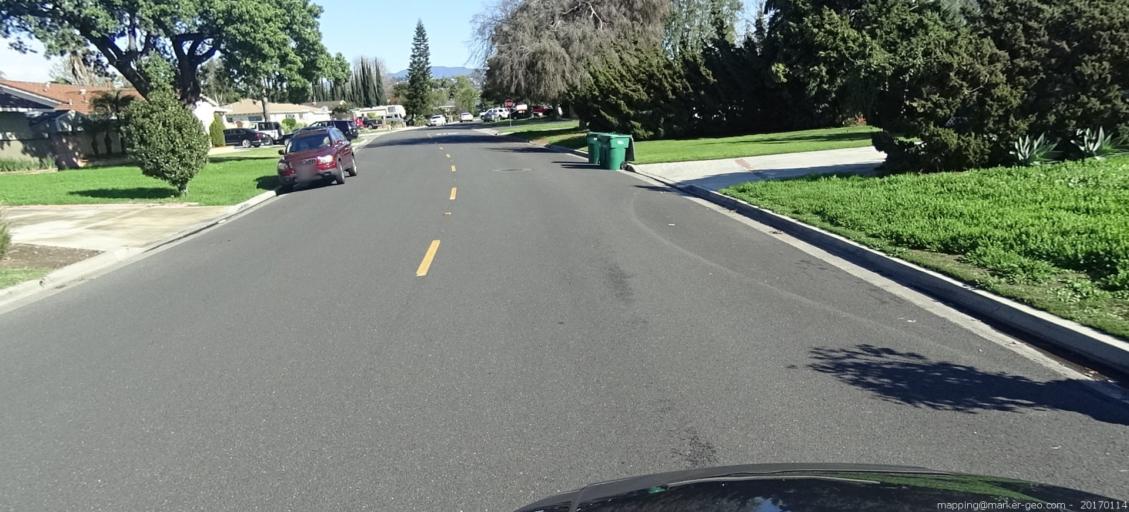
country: US
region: California
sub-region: Orange County
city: Tustin
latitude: 33.7528
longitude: -117.8189
